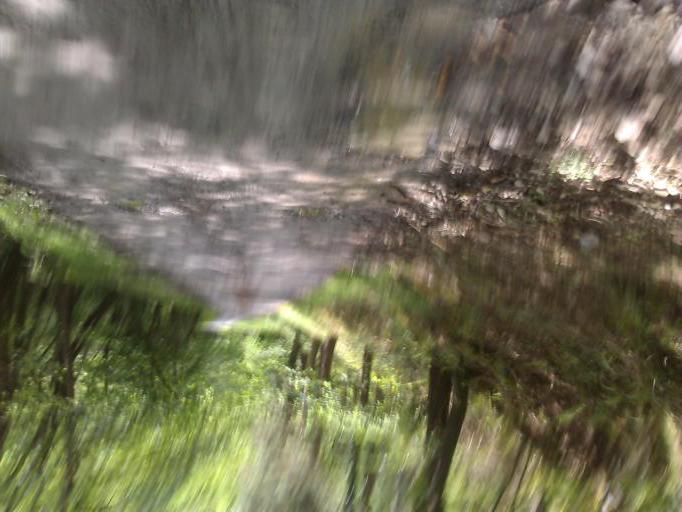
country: ES
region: Basque Country
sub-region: Provincia de Guipuzcoa
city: Berastegui
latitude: 43.1378
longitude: -1.9492
